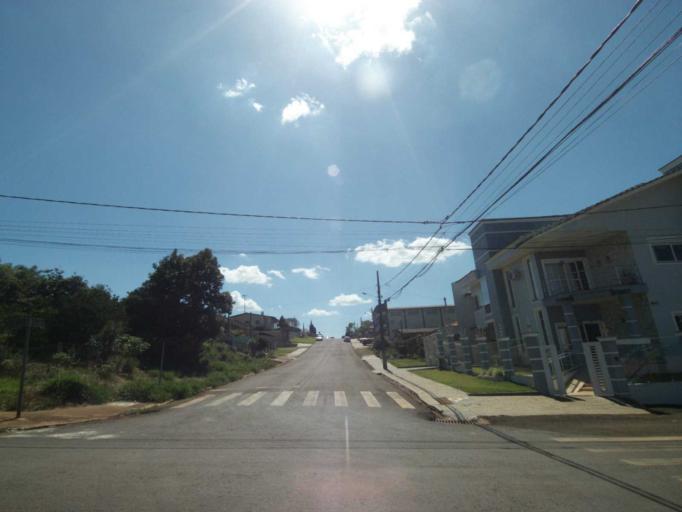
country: BR
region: Parana
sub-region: Laranjeiras Do Sul
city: Laranjeiras do Sul
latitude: -25.3794
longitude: -52.2025
